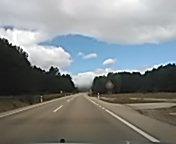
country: ES
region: Castille and Leon
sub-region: Provincia de Soria
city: San Leonardo de Yague
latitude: 41.8395
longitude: -3.0937
